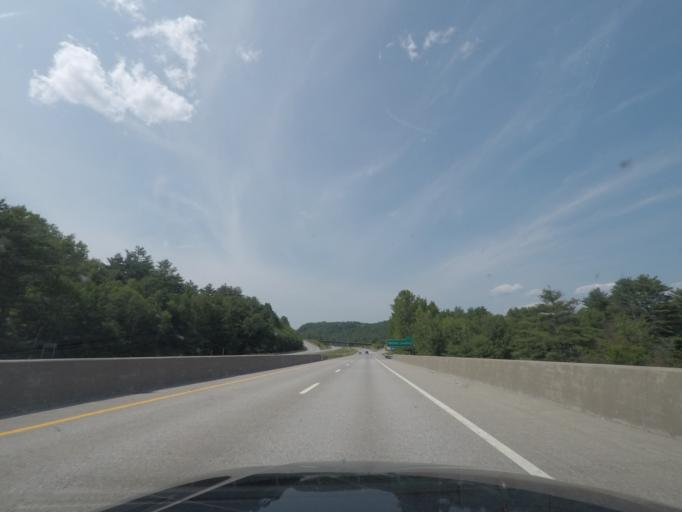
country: US
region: New York
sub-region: Warren County
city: Warrensburg
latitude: 43.5997
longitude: -73.7288
